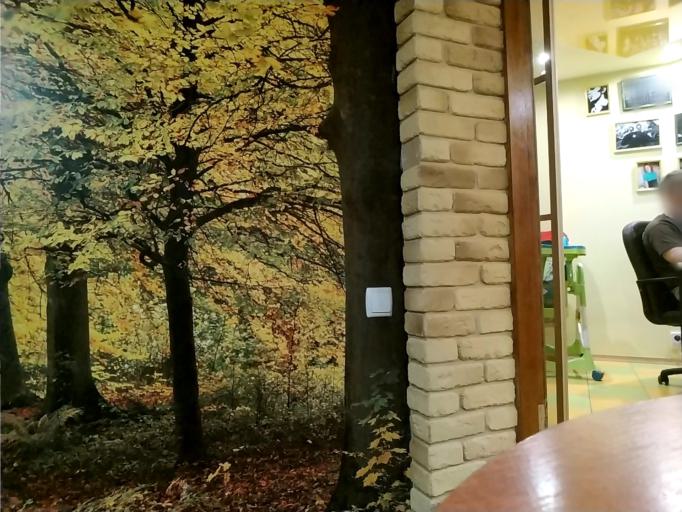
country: RU
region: Tverskaya
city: Zapadnaya Dvina
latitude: 56.3226
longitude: 31.9187
